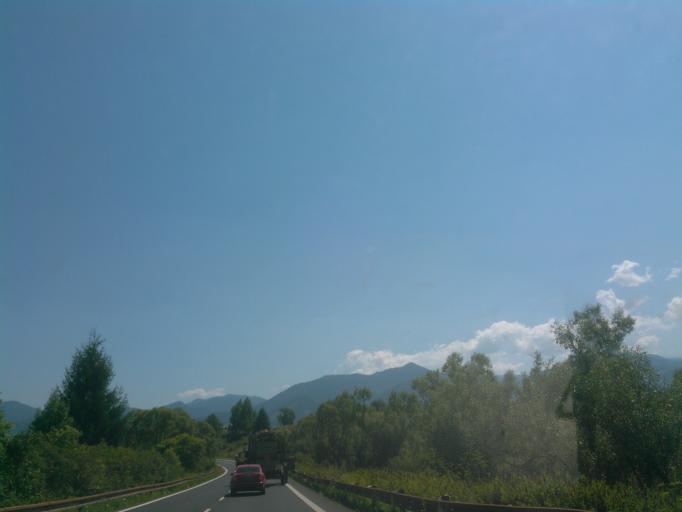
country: SK
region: Zilinsky
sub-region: Okres Liptovsky Mikulas
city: Liptovsky Mikulas
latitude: 49.0569
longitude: 19.4929
